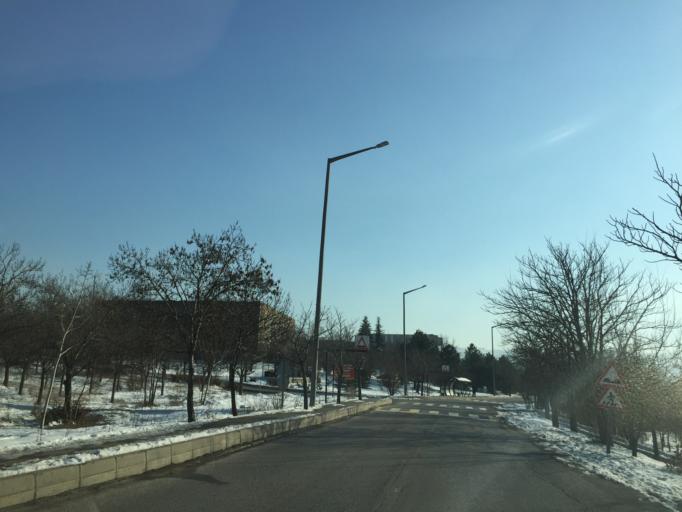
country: TR
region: Ankara
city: Ankara
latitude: 39.8989
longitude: 32.7807
